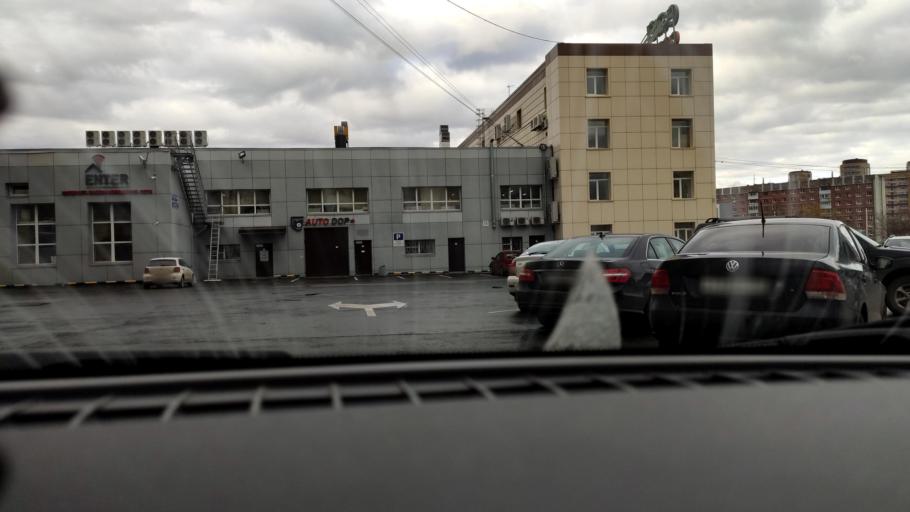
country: RU
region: Perm
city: Perm
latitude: 57.9893
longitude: 56.2054
